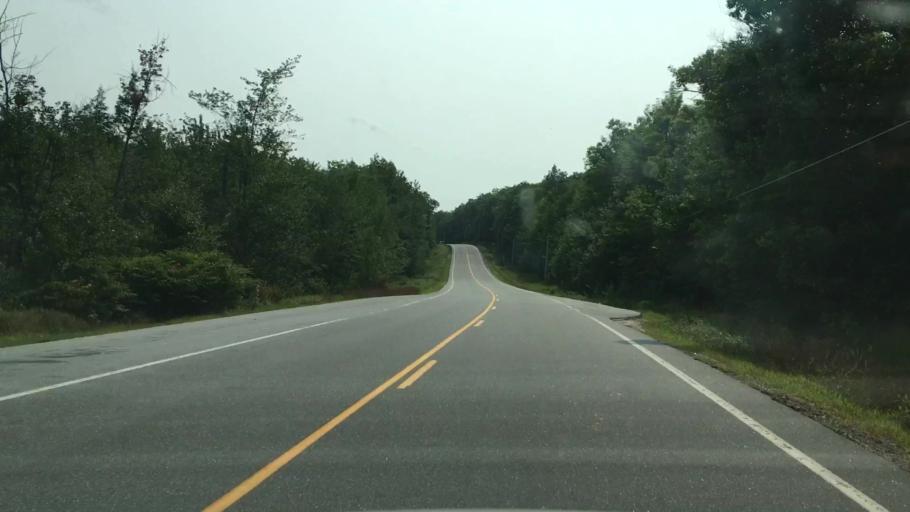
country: US
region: Maine
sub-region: Oxford County
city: Paris
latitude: 44.2610
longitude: -70.4357
